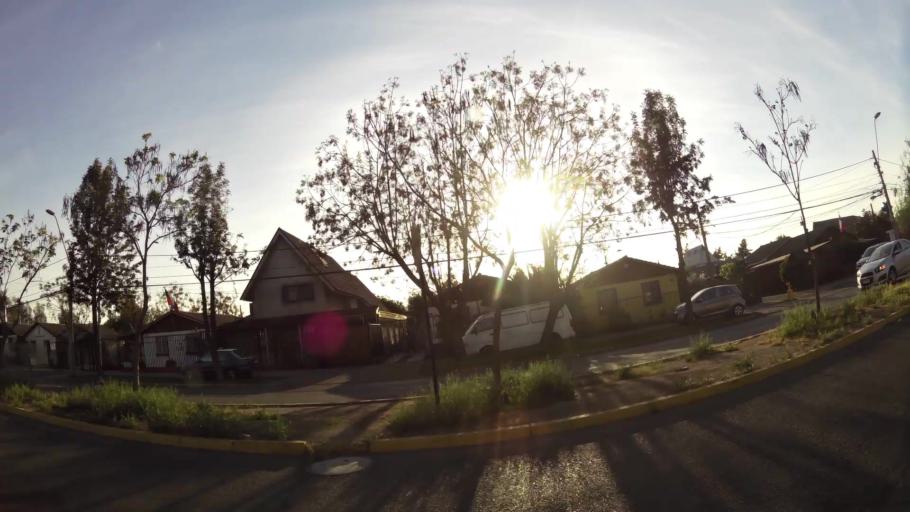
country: CL
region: Santiago Metropolitan
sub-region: Provincia de Cordillera
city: Puente Alto
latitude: -33.5466
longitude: -70.5790
